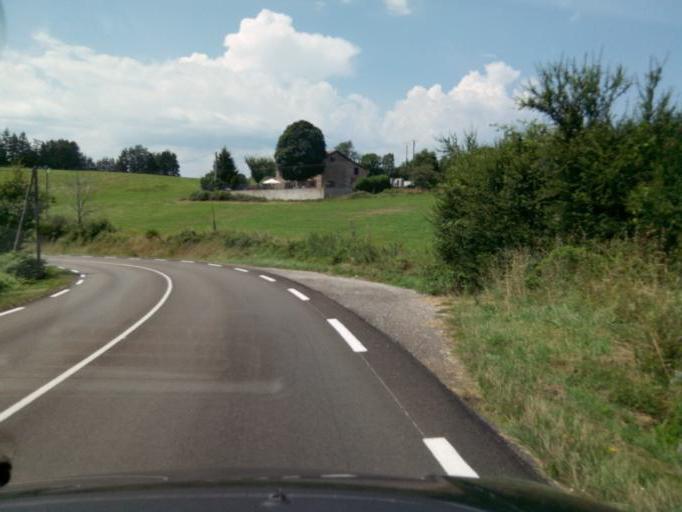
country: FR
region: Rhone-Alpes
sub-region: Departement de la Loire
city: La Ricamarie
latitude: 45.4143
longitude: 4.2928
